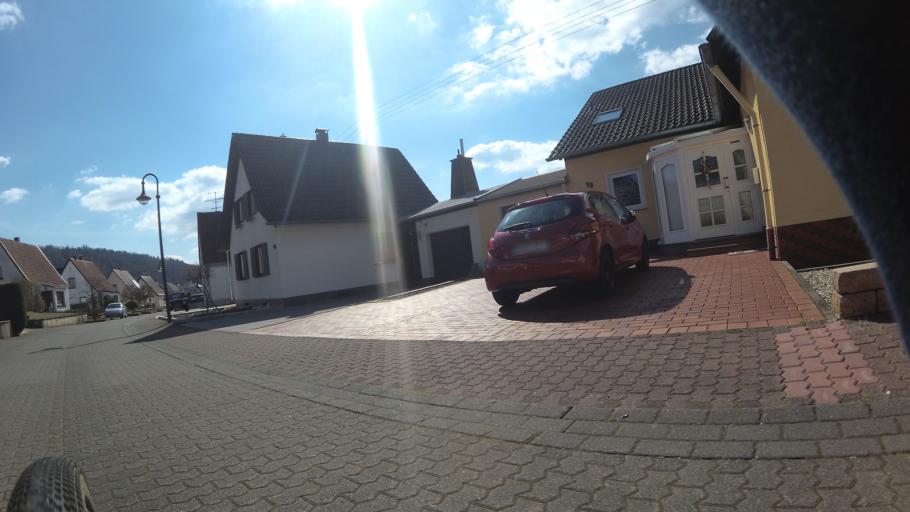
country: DE
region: Saarland
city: Rehlingen-Siersburg
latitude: 49.3666
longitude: 6.6721
